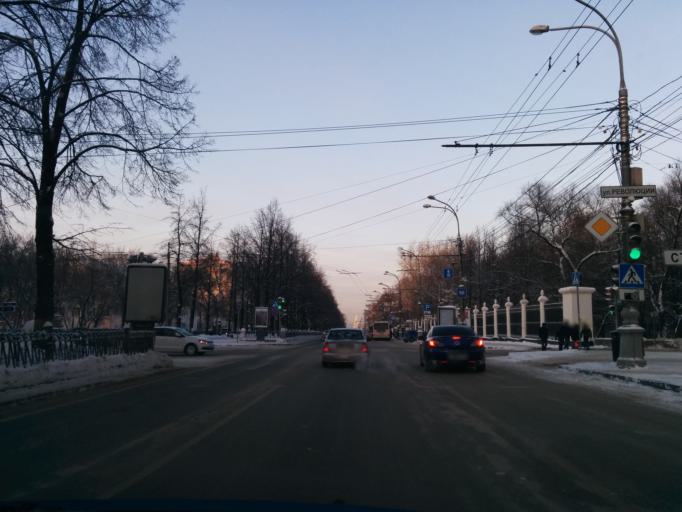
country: RU
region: Perm
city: Perm
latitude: 58.0023
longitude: 56.2478
